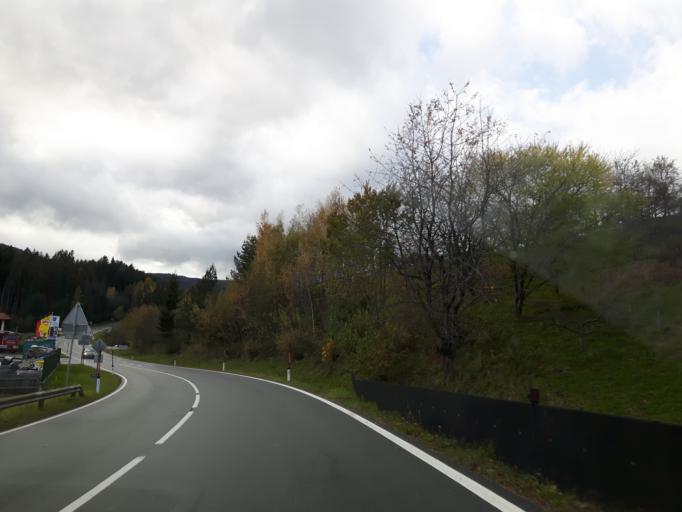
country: AT
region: Styria
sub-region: Politischer Bezirk Deutschlandsberg
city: Sankt Oswald ob Eibiswald
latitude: 46.7065
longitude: 15.1436
